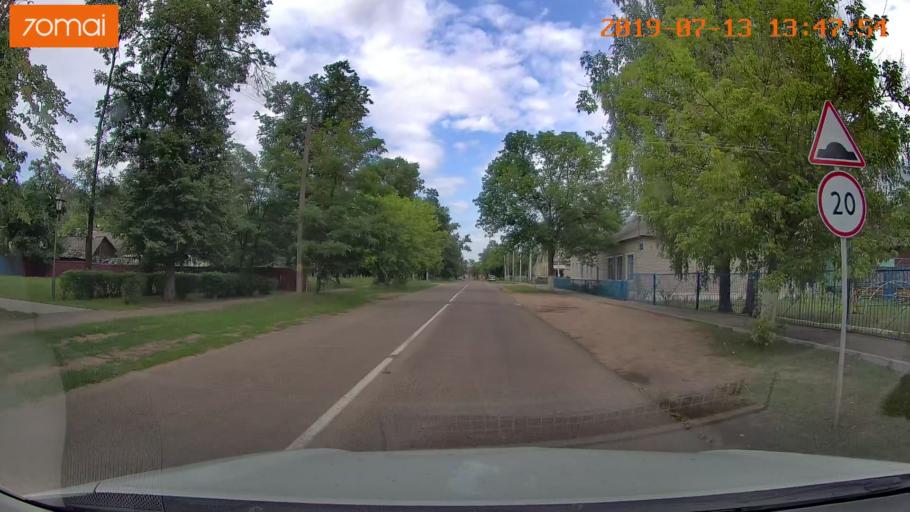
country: BY
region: Mogilev
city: Asipovichy
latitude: 53.2969
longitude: 28.6409
